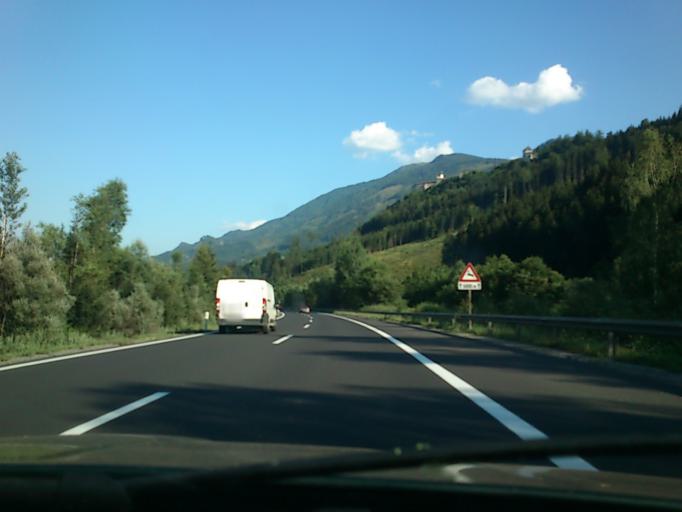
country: AT
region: Styria
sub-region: Politischer Bezirk Liezen
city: Selzthal
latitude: 47.5354
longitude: 14.3096
